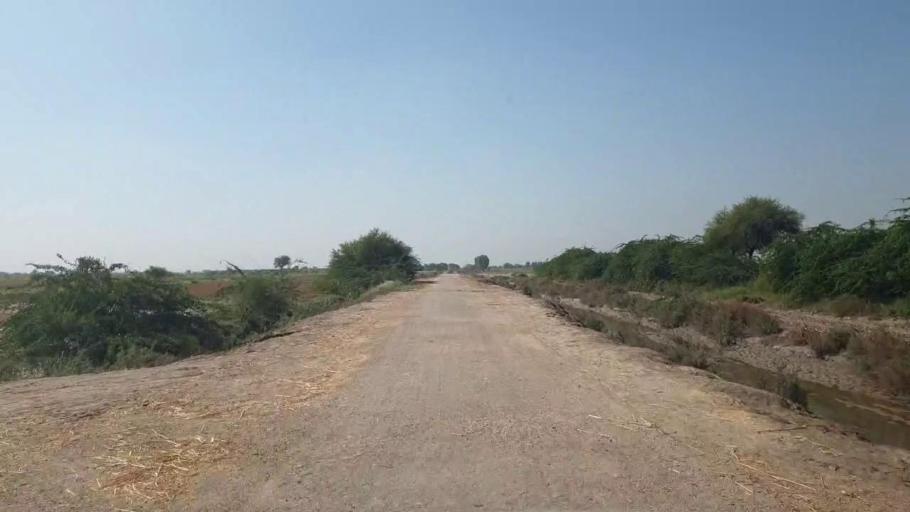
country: PK
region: Sindh
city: Talhar
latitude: 24.8193
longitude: 68.7621
